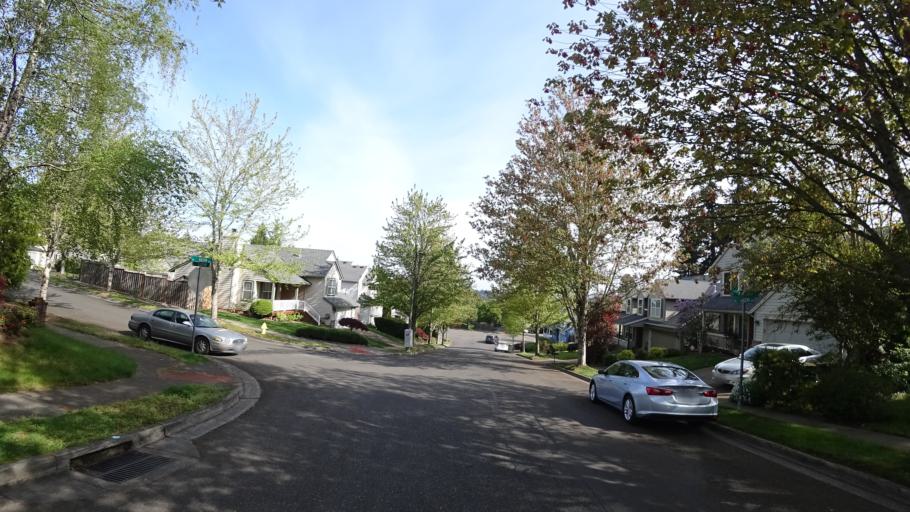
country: US
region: Oregon
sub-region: Washington County
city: Beaverton
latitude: 45.4522
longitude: -122.8385
